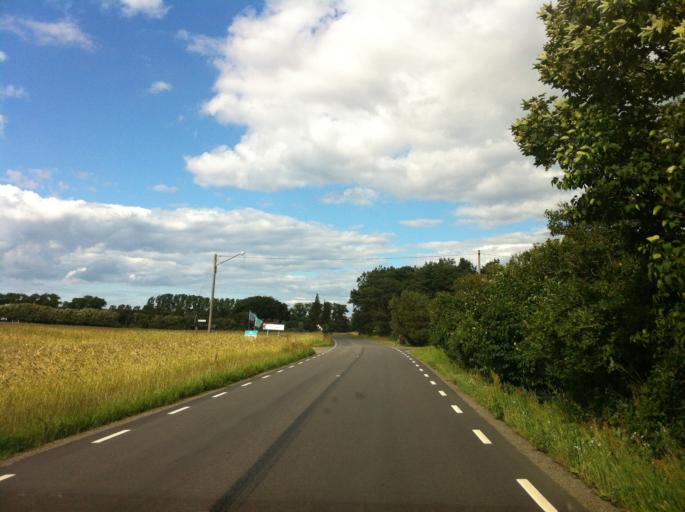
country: SE
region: Skane
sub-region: Simrishamns Kommun
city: Simrishamn
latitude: 55.4418
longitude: 14.2381
